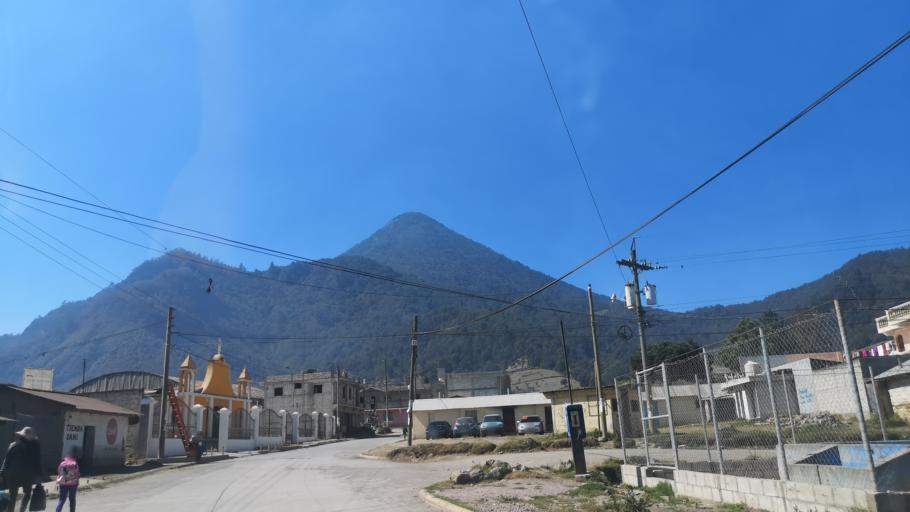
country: GT
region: Quetzaltenango
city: Quetzaltenango
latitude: 14.7916
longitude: -91.5437
